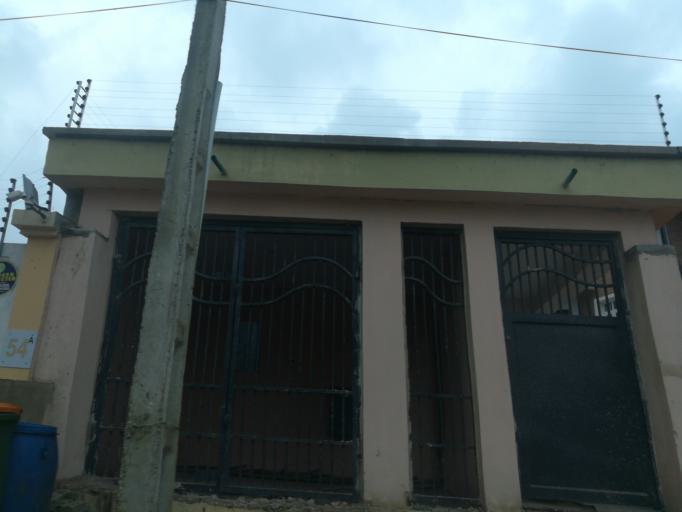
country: NG
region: Lagos
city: Oshodi
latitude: 6.5718
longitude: 3.3504
